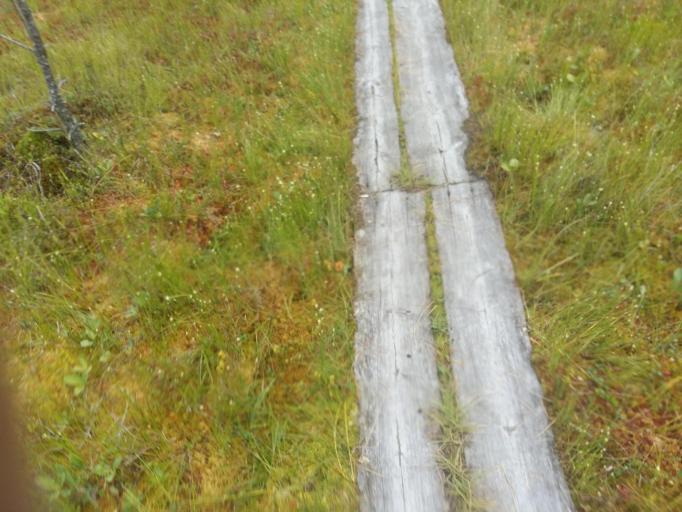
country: LT
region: Alytaus apskritis
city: Druskininkai
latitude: 54.0381
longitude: 24.2785
